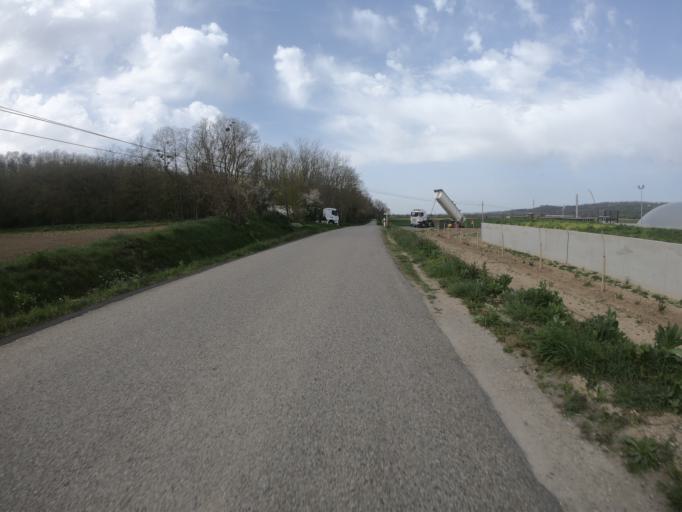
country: FR
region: Midi-Pyrenees
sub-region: Departement de l'Ariege
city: La Tour-du-Crieu
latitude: 43.1193
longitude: 1.7213
